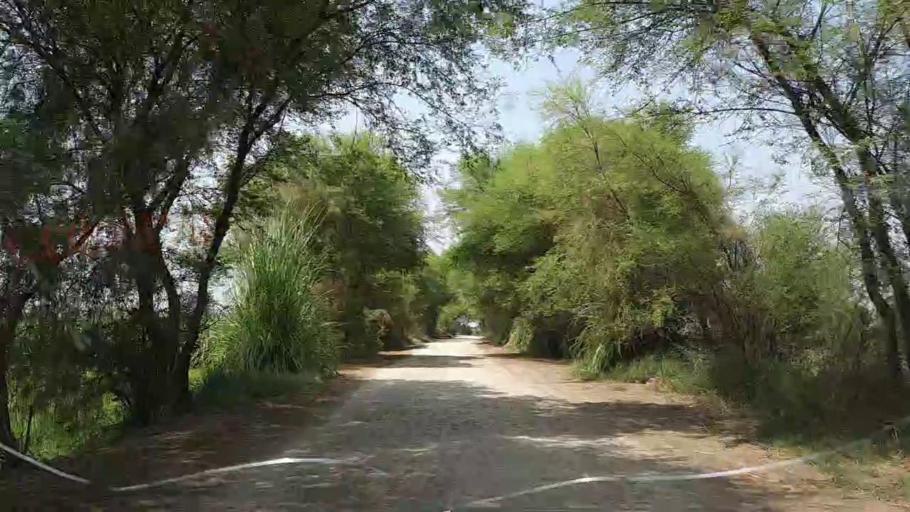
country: PK
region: Sindh
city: Ghotki
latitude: 28.0807
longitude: 69.3190
